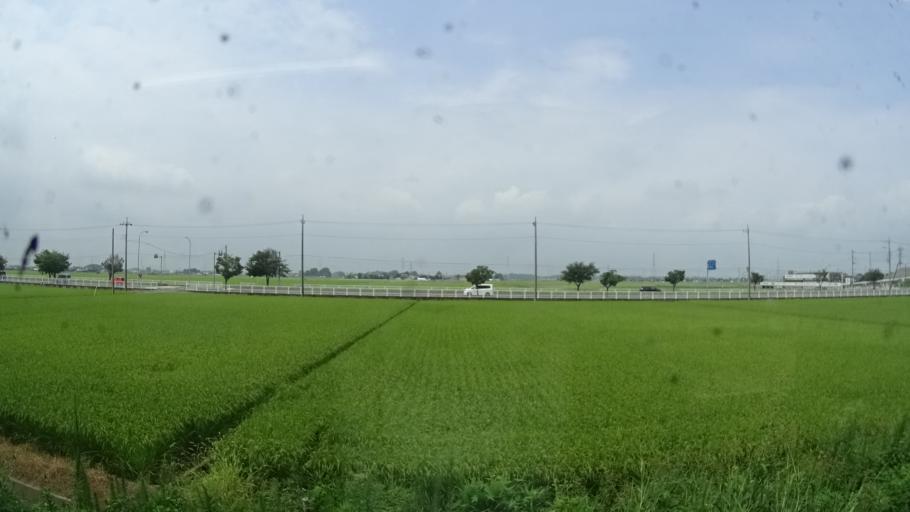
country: JP
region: Ibaraki
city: Shimodate
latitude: 36.3345
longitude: 139.9722
